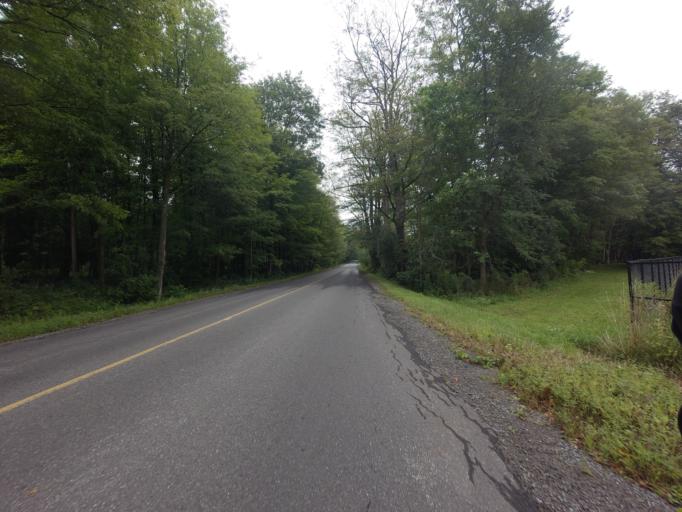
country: CA
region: Ontario
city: Bells Corners
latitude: 45.3394
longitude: -75.9920
